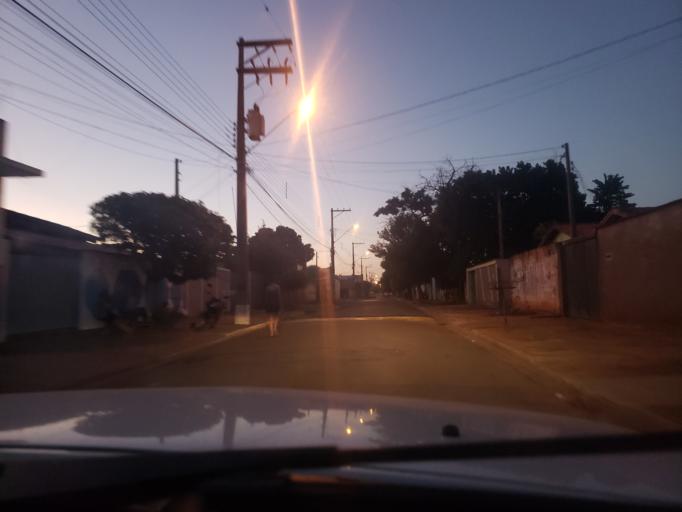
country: BR
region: Sao Paulo
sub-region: Conchal
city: Conchal
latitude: -22.2960
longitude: -47.1316
